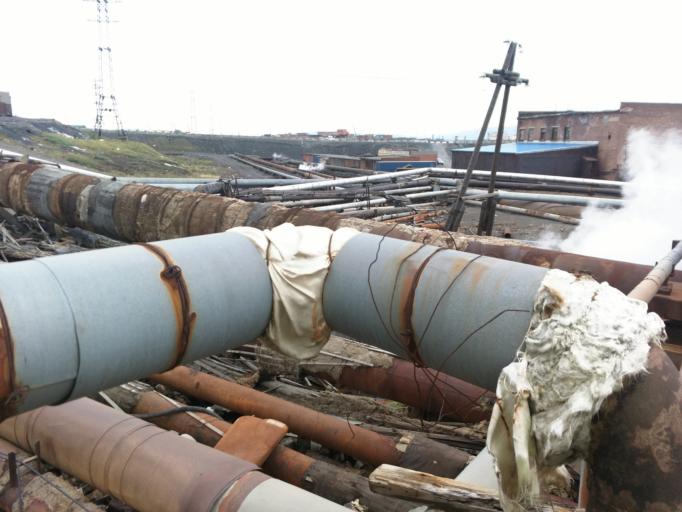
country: RU
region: Krasnoyarskiy
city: Norilsk
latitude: 69.3556
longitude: 88.1548
